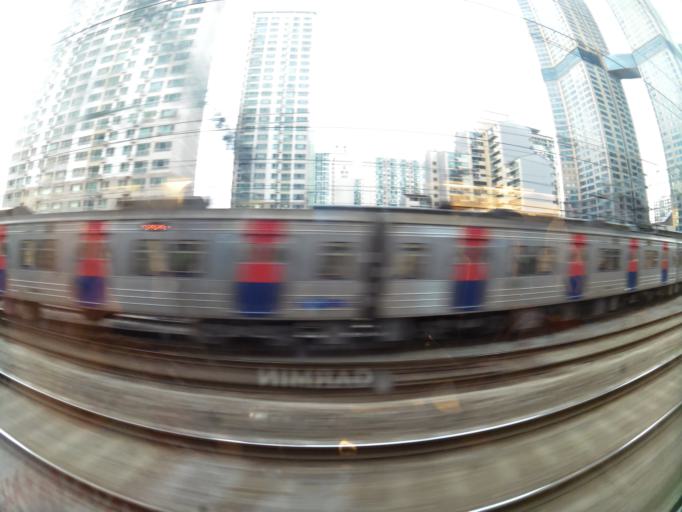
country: KR
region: Gyeonggi-do
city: Kwangmyong
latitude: 37.5066
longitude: 126.8873
